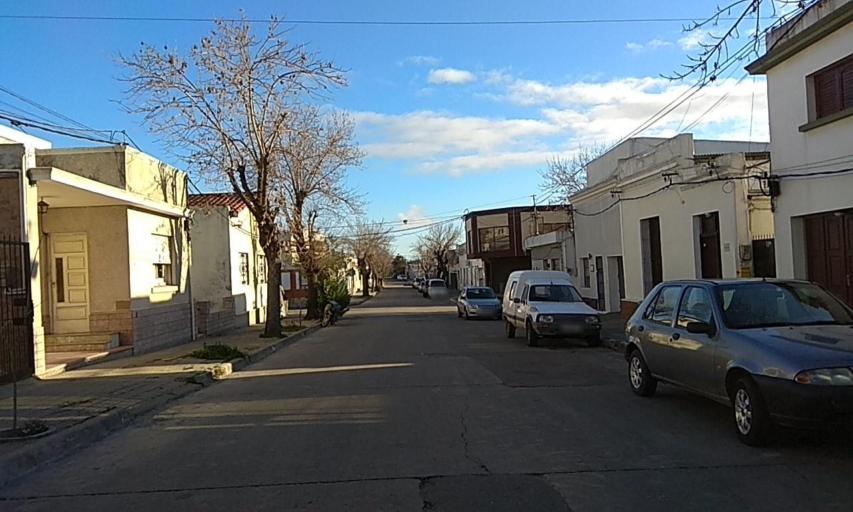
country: UY
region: Florida
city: Florida
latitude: -34.0964
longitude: -56.2193
